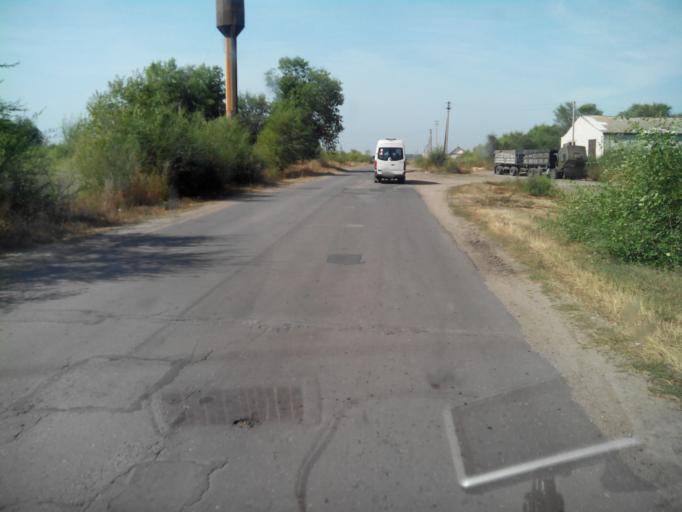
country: RU
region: Samara
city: Balasheyka
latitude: 53.1541
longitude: 48.1020
